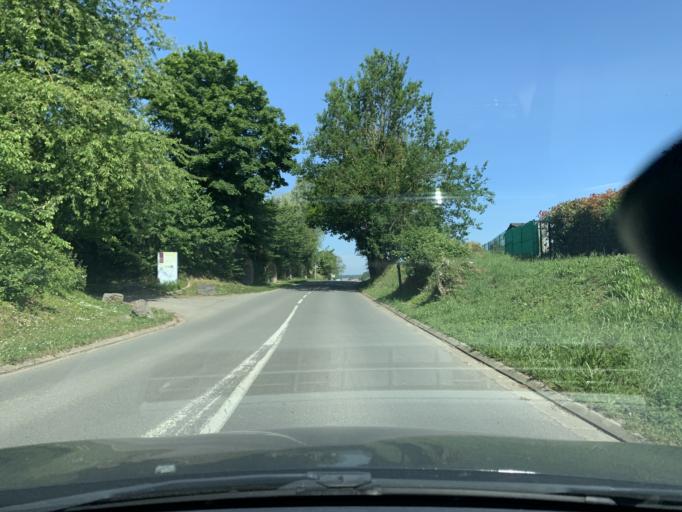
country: FR
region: Nord-Pas-de-Calais
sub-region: Departement du Nord
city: Marcoing
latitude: 50.1408
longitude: 3.1762
